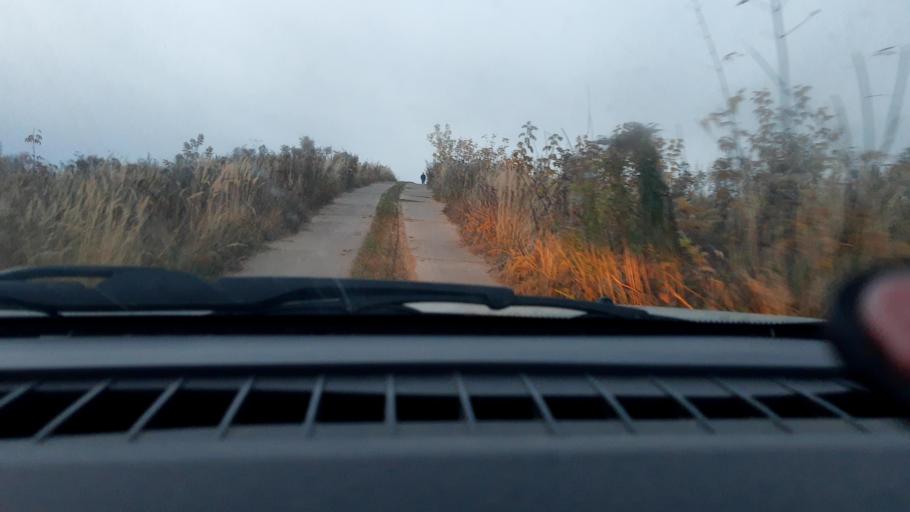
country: RU
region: Nizjnij Novgorod
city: Nizhniy Novgorod
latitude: 56.2321
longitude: 43.9932
